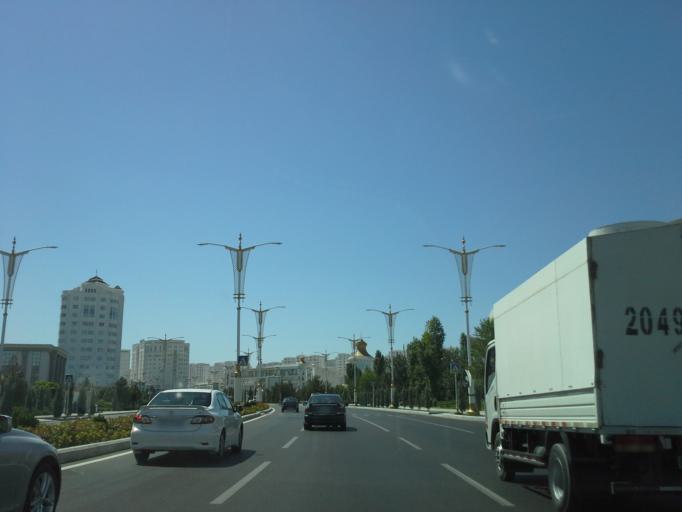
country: TM
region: Ahal
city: Ashgabat
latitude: 37.9156
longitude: 58.3750
